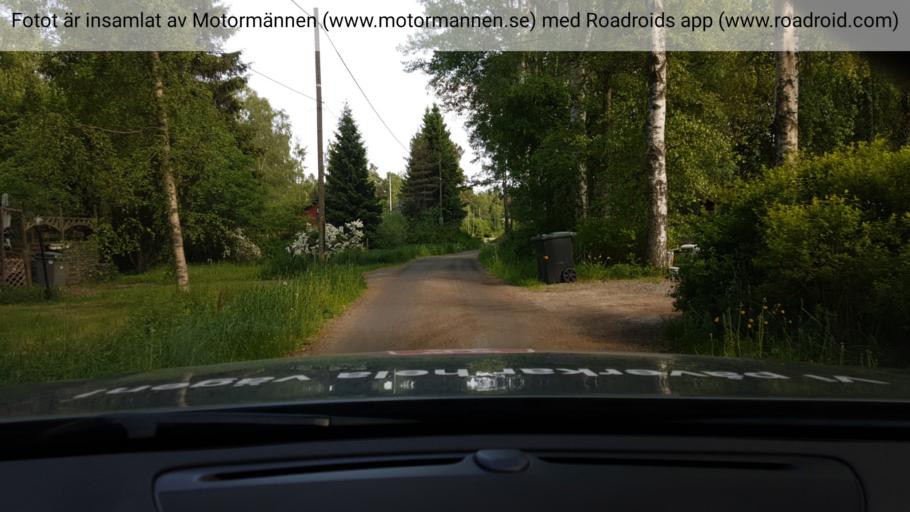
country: SE
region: Stockholm
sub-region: Varmdo Kommun
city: Mortnas
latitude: 59.2471
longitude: 18.4581
